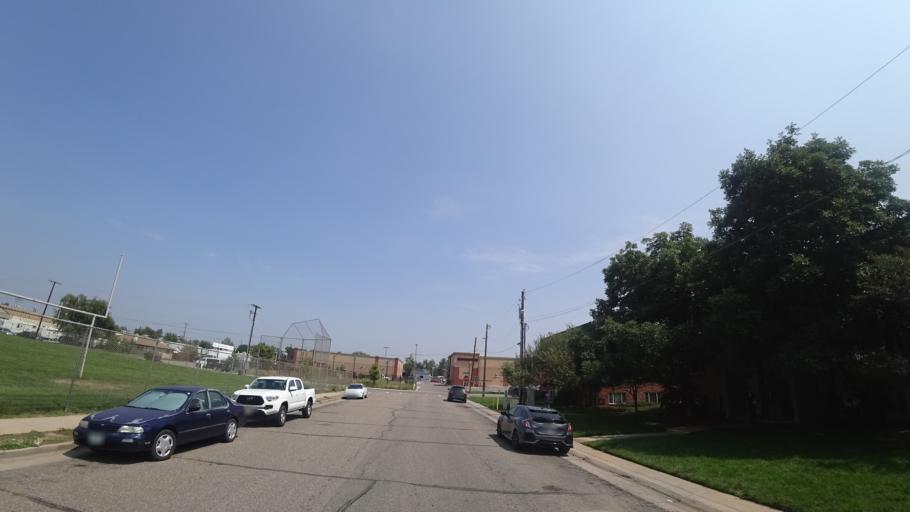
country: US
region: Colorado
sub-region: Arapahoe County
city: Englewood
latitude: 39.6259
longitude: -104.9899
